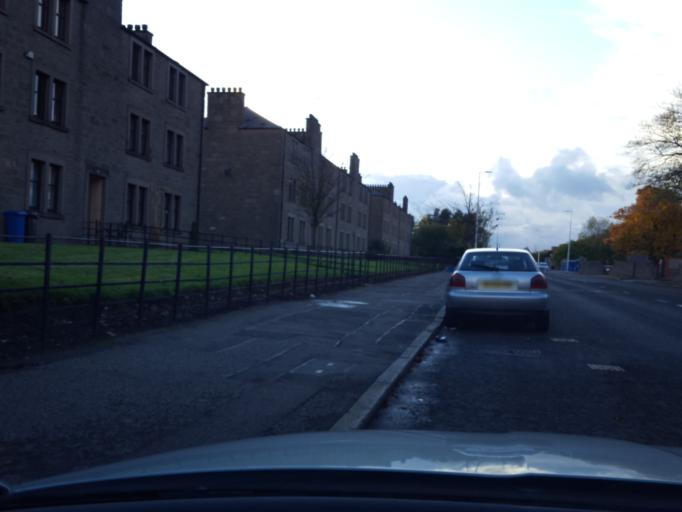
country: GB
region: Scotland
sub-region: Dundee City
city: Dundee
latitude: 56.4750
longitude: -2.9864
